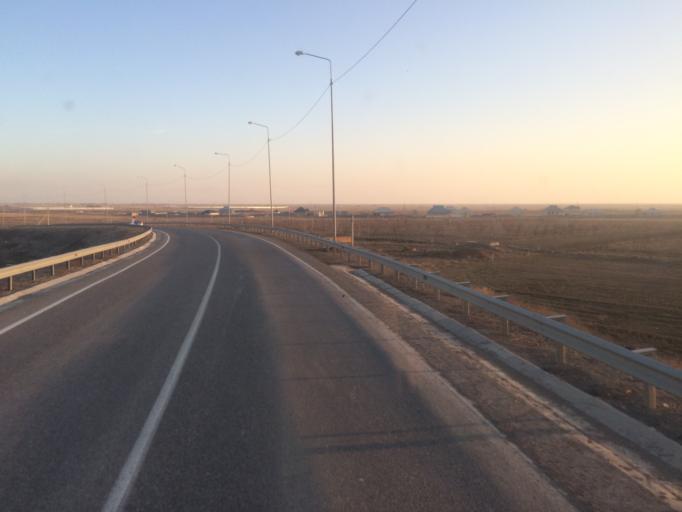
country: KZ
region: Ongtustik Qazaqstan
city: Turkestan
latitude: 43.2751
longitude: 68.3357
